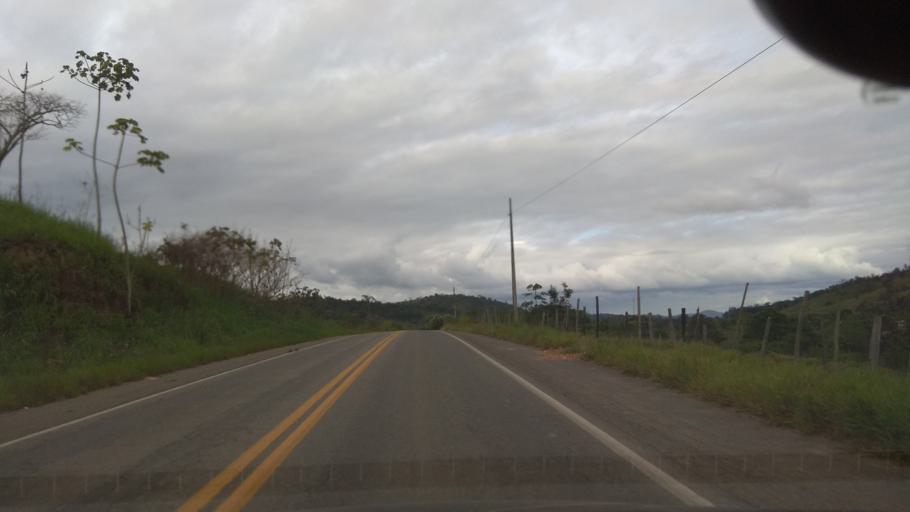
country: BR
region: Bahia
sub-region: Ipiau
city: Ipiau
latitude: -14.1443
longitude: -39.7148
